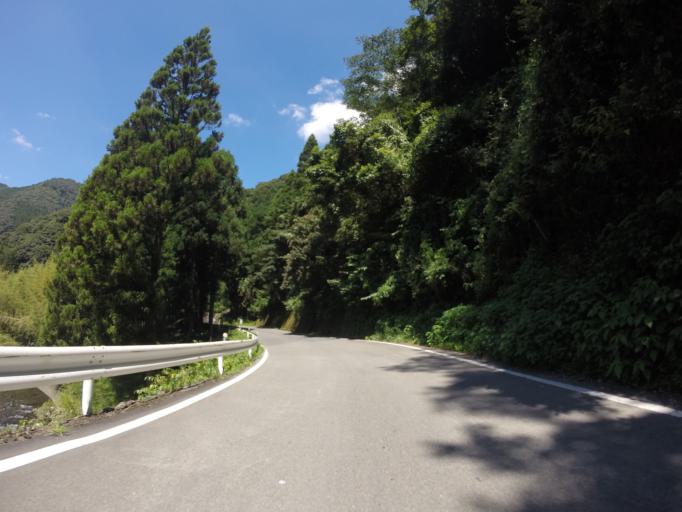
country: JP
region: Shizuoka
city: Shizuoka-shi
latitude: 35.0534
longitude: 138.2408
